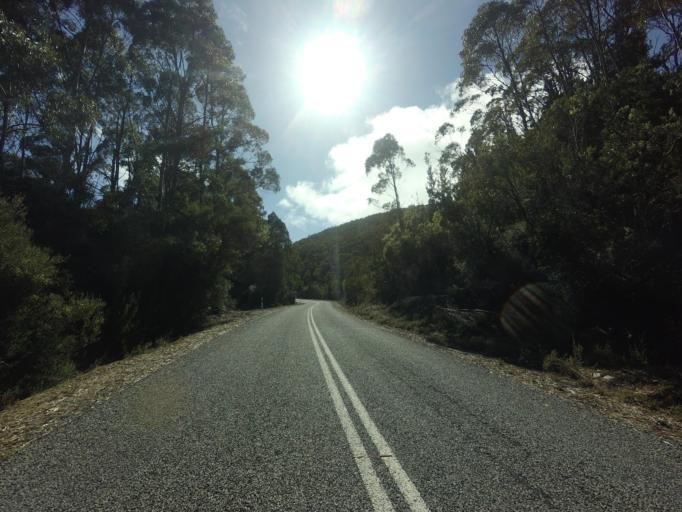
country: AU
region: Tasmania
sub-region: Huon Valley
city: Geeveston
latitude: -42.8074
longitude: 146.3929
